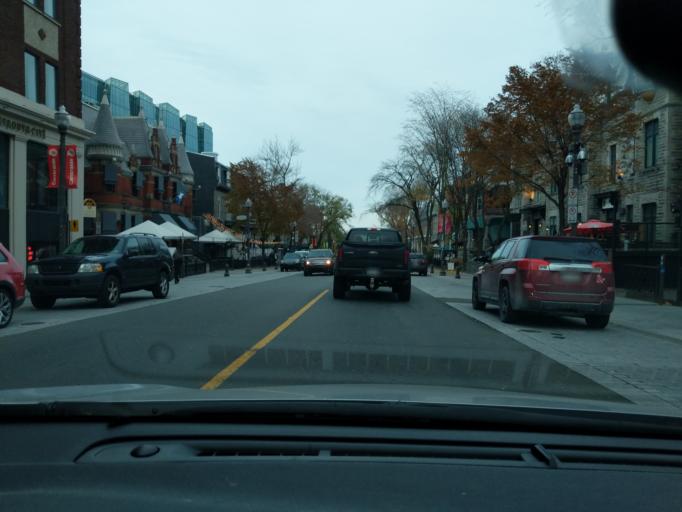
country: CA
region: Quebec
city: Quebec
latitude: 46.8059
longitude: -71.2172
